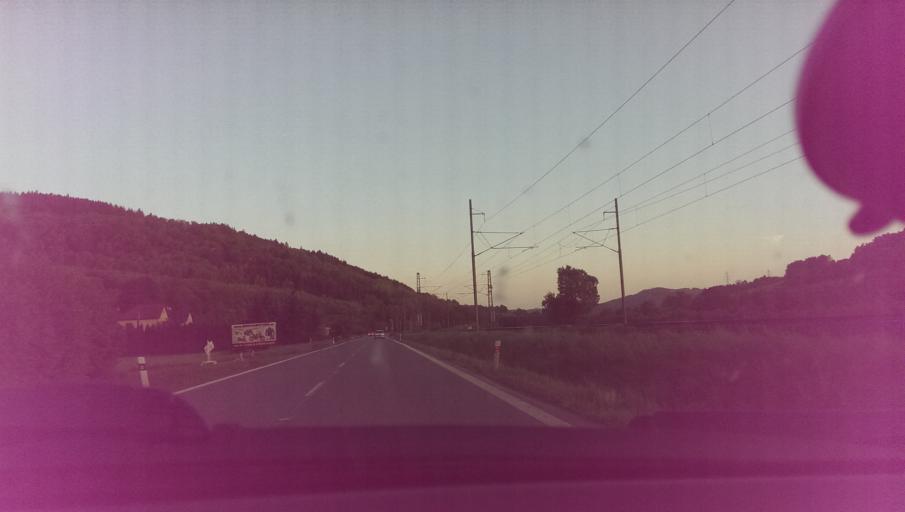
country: CZ
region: Zlin
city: Jablunka
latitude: 49.4112
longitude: 17.9528
